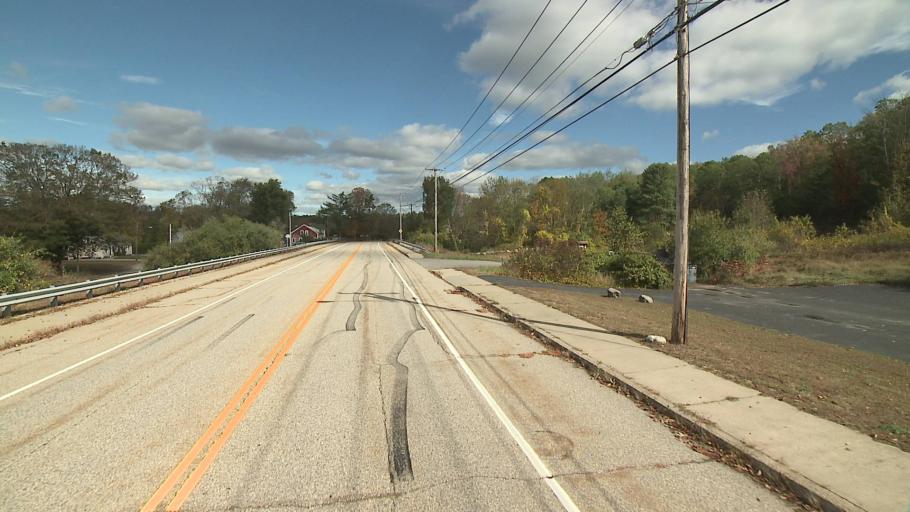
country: US
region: Connecticut
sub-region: Windham County
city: Putnam
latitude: 41.9396
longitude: -71.8943
